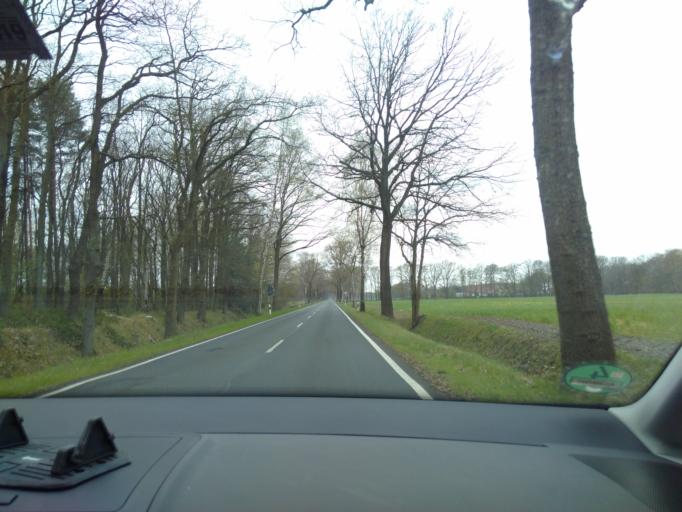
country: DE
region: Lower Saxony
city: Adelheidsdorf
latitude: 52.5889
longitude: 10.0405
